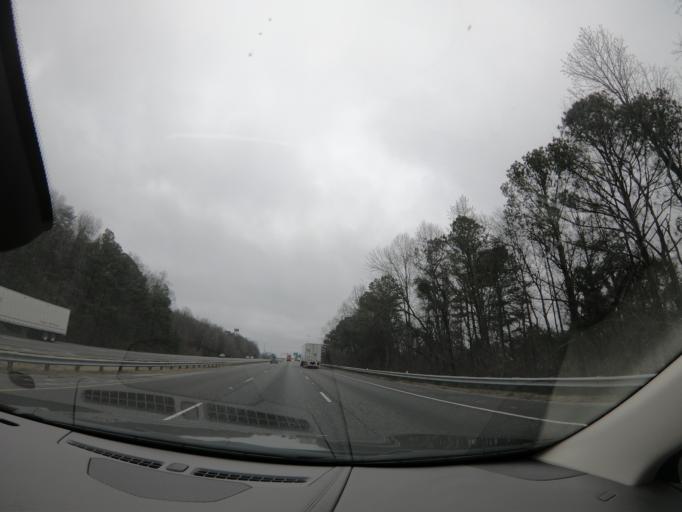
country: US
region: Georgia
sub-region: Whitfield County
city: Dalton
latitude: 34.7549
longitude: -85.0022
